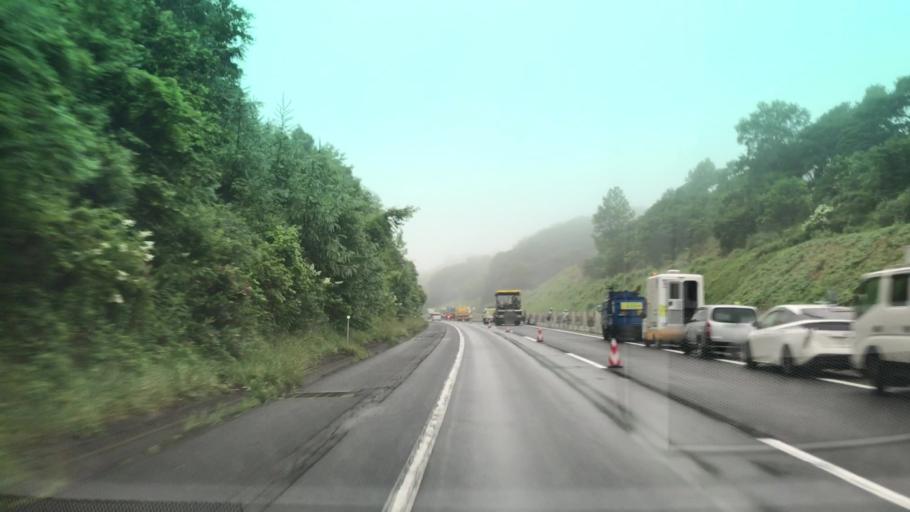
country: JP
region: Hokkaido
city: Tomakomai
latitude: 42.6639
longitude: 141.5883
